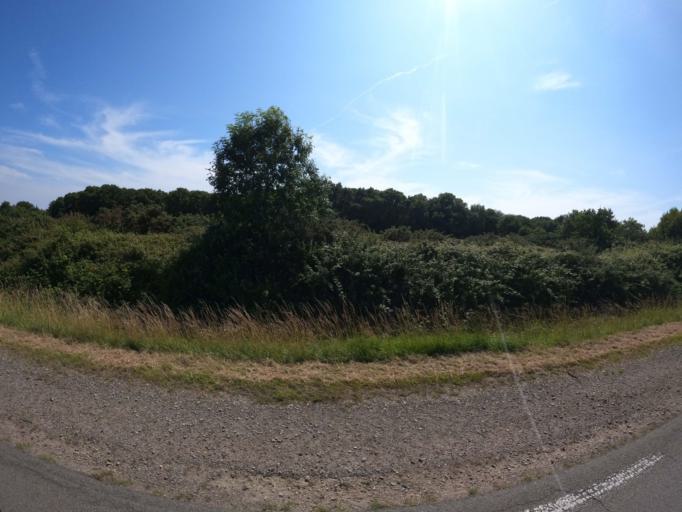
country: FR
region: Pays de la Loire
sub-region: Departement de la Loire-Atlantique
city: La Bernerie-en-Retz
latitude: 47.1025
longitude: -2.0421
